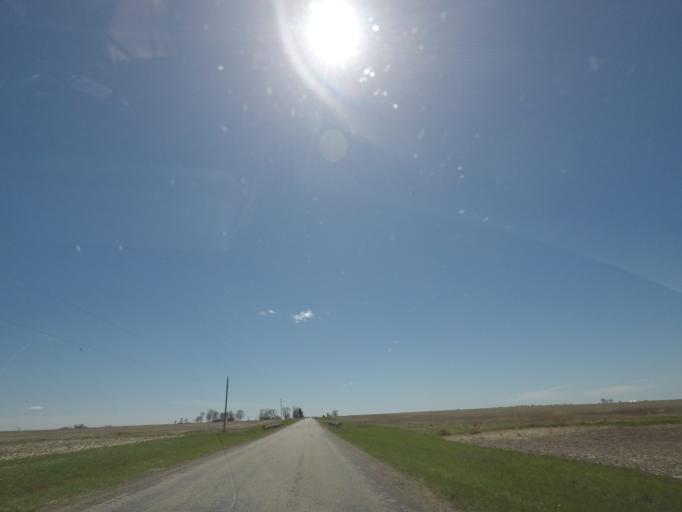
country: US
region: Illinois
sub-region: Logan County
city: Atlanta
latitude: 40.1759
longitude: -89.1939
